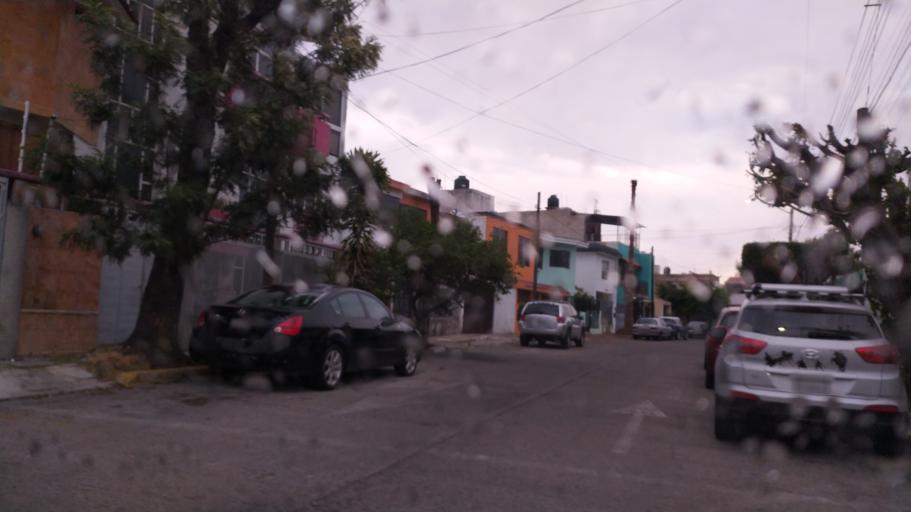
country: MX
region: Jalisco
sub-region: Zapopan
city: Zapopan
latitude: 20.7198
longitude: -103.3664
